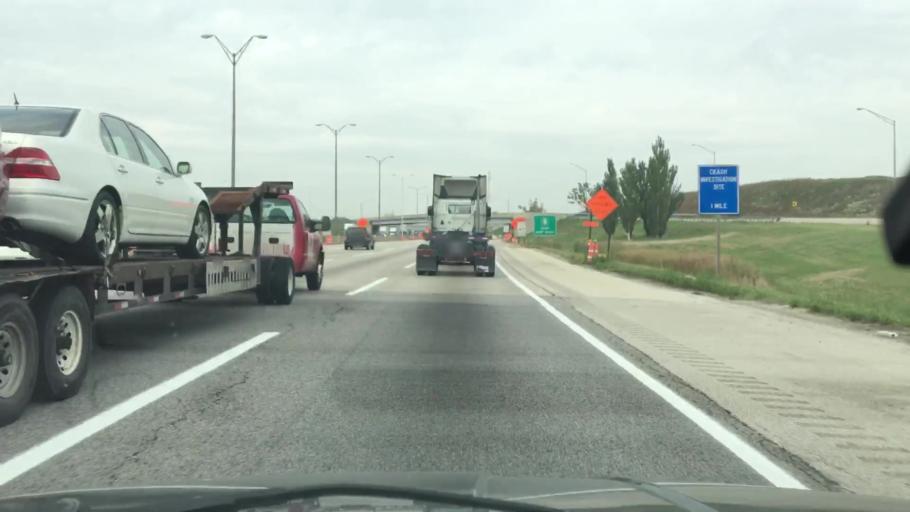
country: US
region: Illinois
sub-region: DuPage County
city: Oak Brook
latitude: 41.8411
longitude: -87.9194
